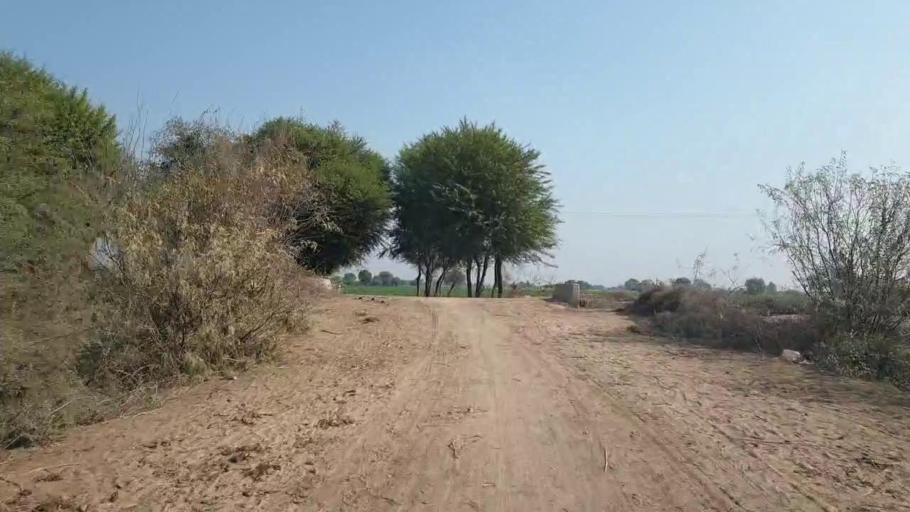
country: PK
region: Sindh
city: Hala
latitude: 25.9186
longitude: 68.4012
